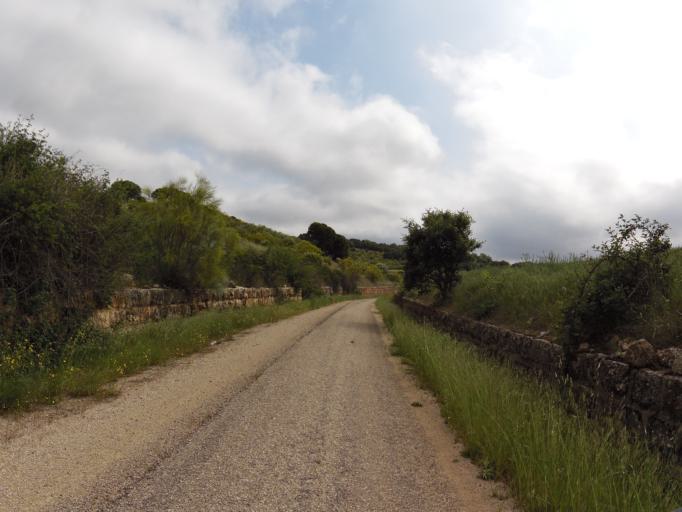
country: ES
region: Castille-La Mancha
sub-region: Provincia de Albacete
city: Alcaraz
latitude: 38.7182
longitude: -2.4899
